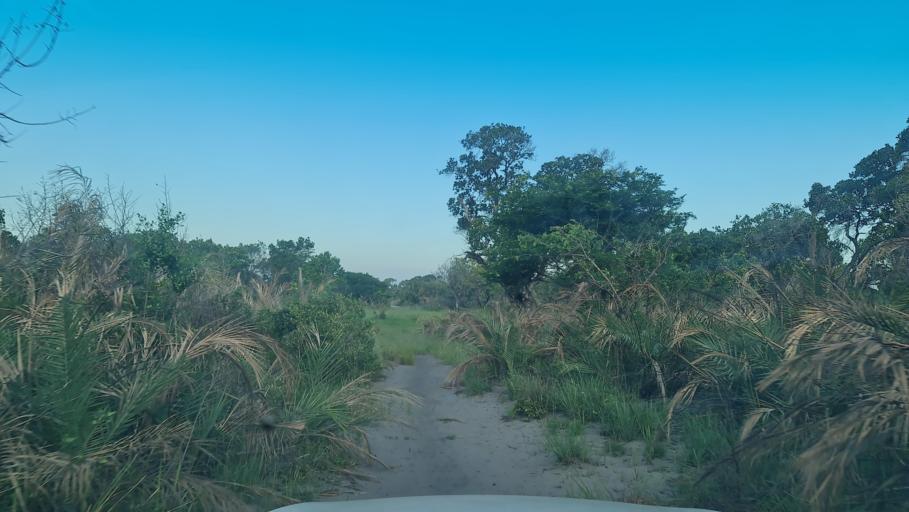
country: MZ
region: Gaza
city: Macia
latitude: -25.2176
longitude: 33.0460
